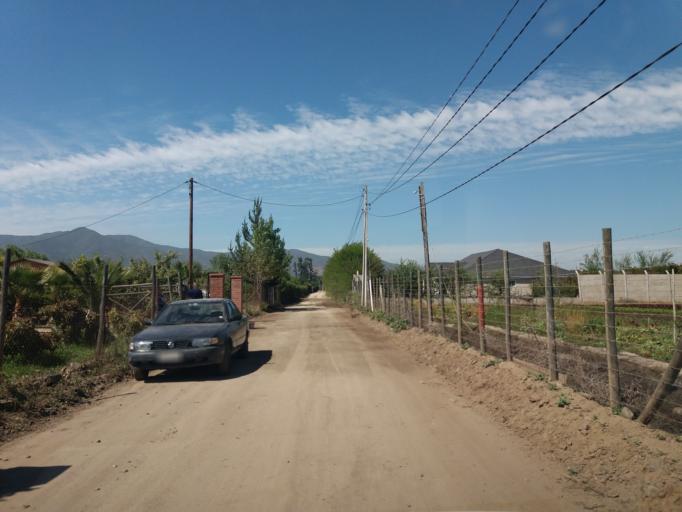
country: CL
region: Valparaiso
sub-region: Provincia de Quillota
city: Quillota
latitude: -32.8700
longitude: -71.2238
